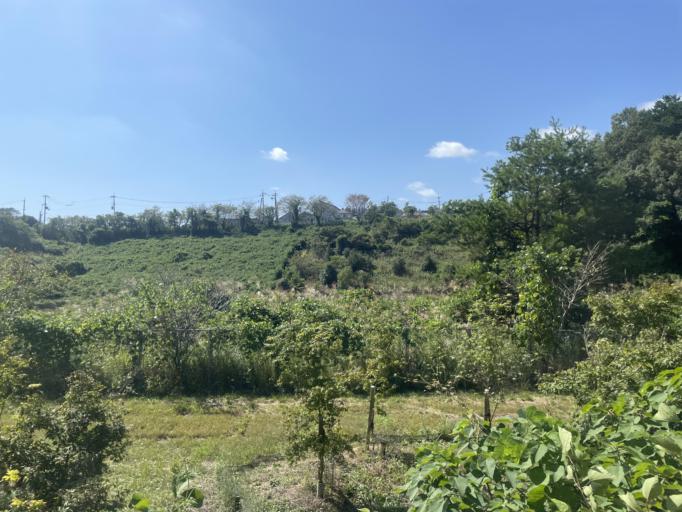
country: JP
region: Nara
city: Gose
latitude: 34.3960
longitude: 135.7488
